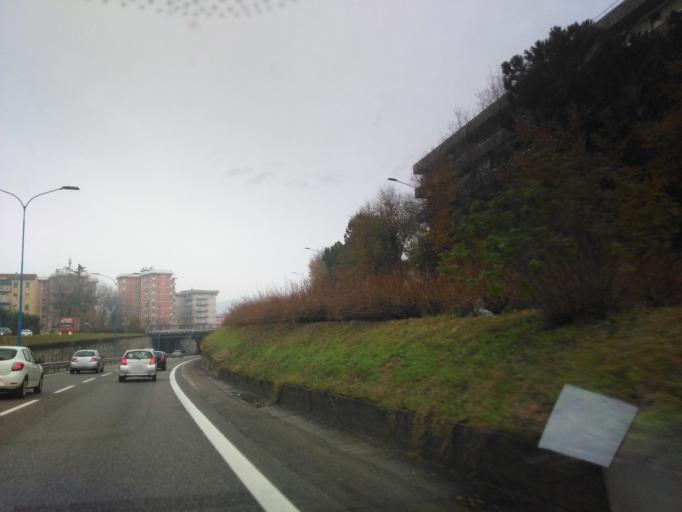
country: IT
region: Lombardy
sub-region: Provincia di Brescia
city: Fantasina
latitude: 45.5454
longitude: 10.1852
